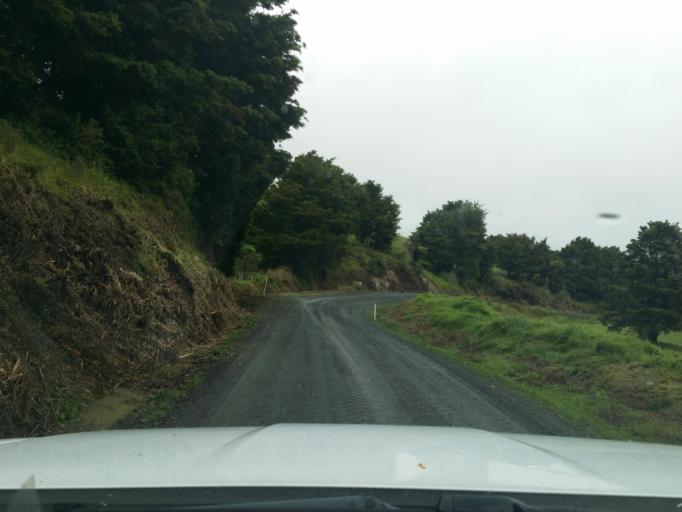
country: NZ
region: Northland
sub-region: Kaipara District
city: Dargaville
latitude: -35.7778
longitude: 173.9482
